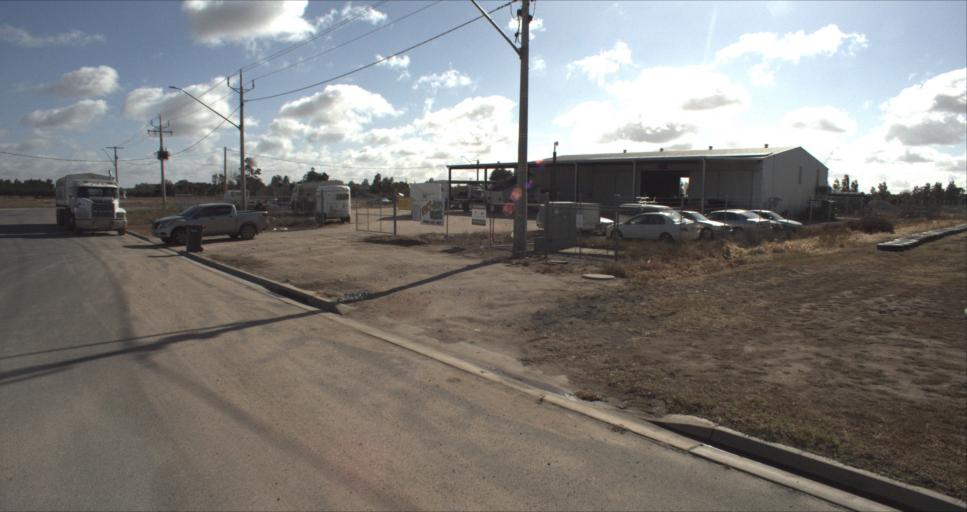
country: AU
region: New South Wales
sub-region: Leeton
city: Leeton
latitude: -34.5462
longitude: 146.3911
